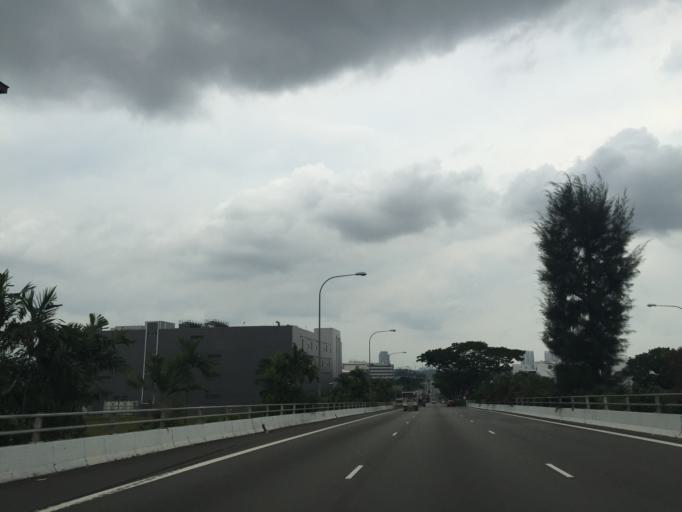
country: SG
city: Singapore
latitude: 1.3219
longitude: 103.7120
